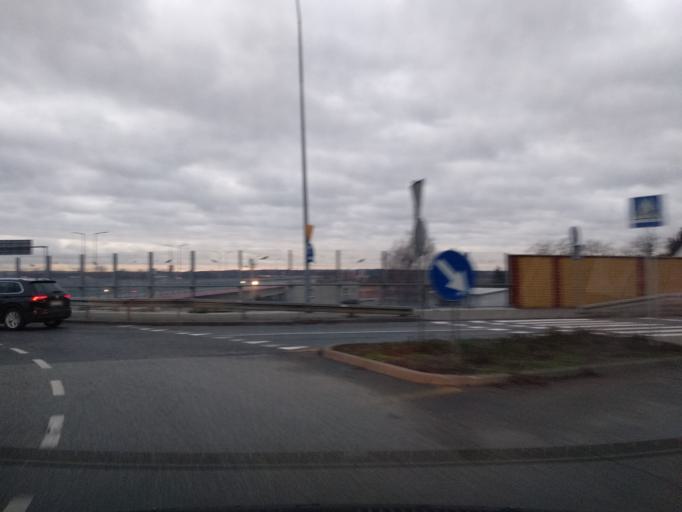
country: PL
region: Greater Poland Voivodeship
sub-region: Konin
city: Konin
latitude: 52.2263
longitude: 18.2438
